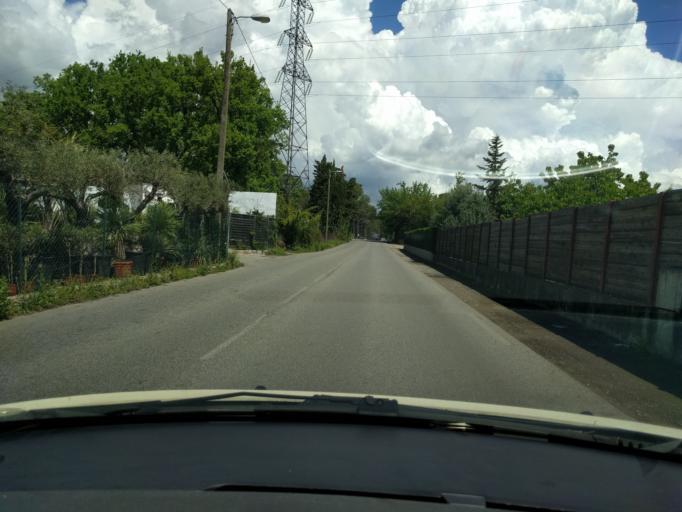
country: FR
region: Provence-Alpes-Cote d'Azur
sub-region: Departement des Alpes-Maritimes
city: La Roquette-sur-Siagne
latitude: 43.6006
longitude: 6.9581
